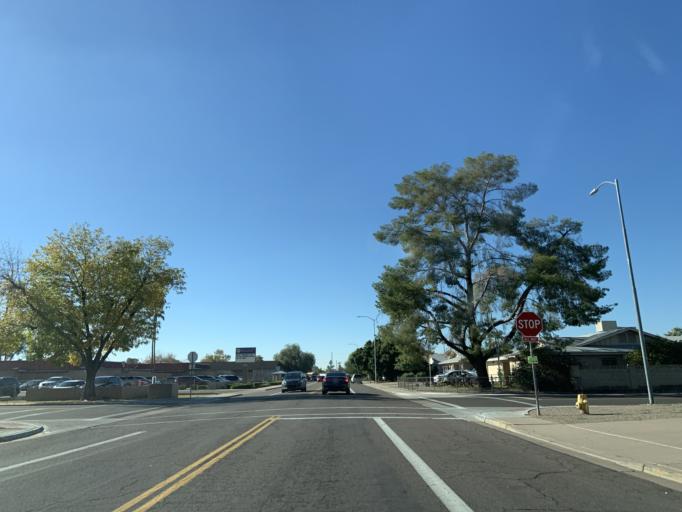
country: US
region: Arizona
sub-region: Maricopa County
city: Tempe
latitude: 33.4003
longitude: -111.8806
